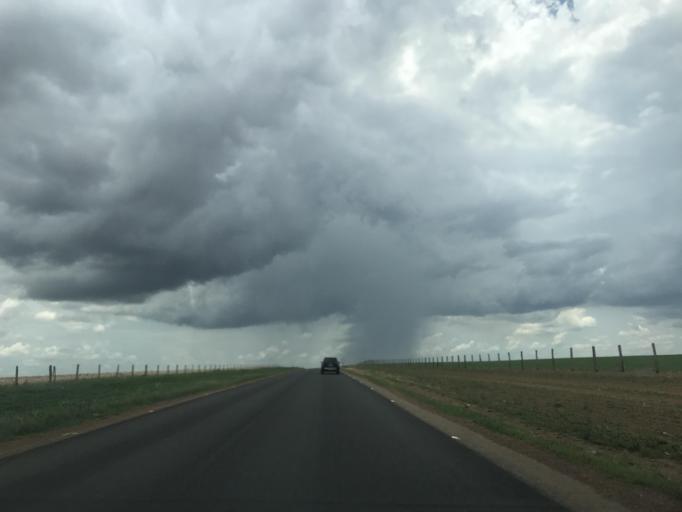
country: BR
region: Goias
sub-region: Vianopolis
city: Vianopolis
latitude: -16.8234
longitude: -48.5271
